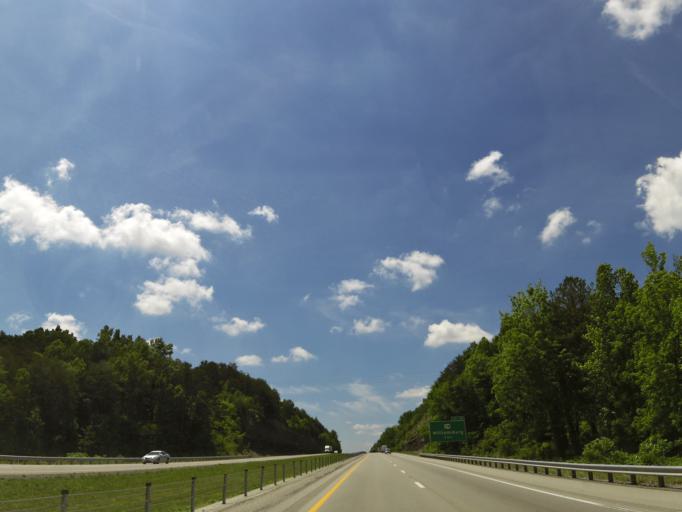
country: US
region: Kentucky
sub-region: Whitley County
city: Williamsburg
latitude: 36.8139
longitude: -84.1663
